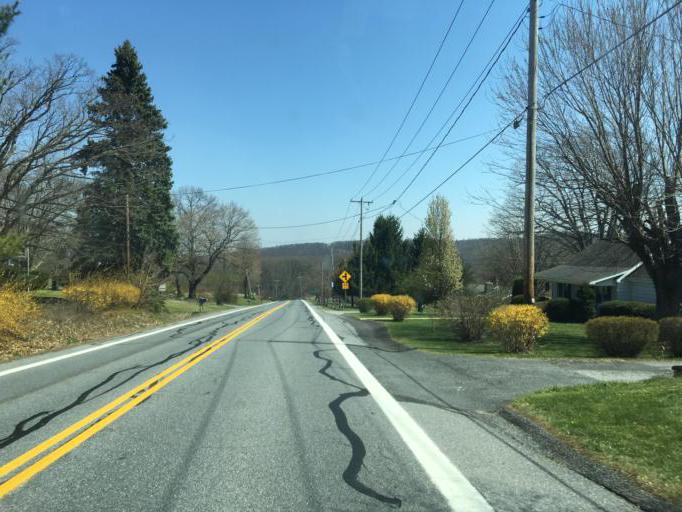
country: US
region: Maryland
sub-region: Washington County
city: Smithsburg
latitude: 39.6371
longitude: -77.5075
